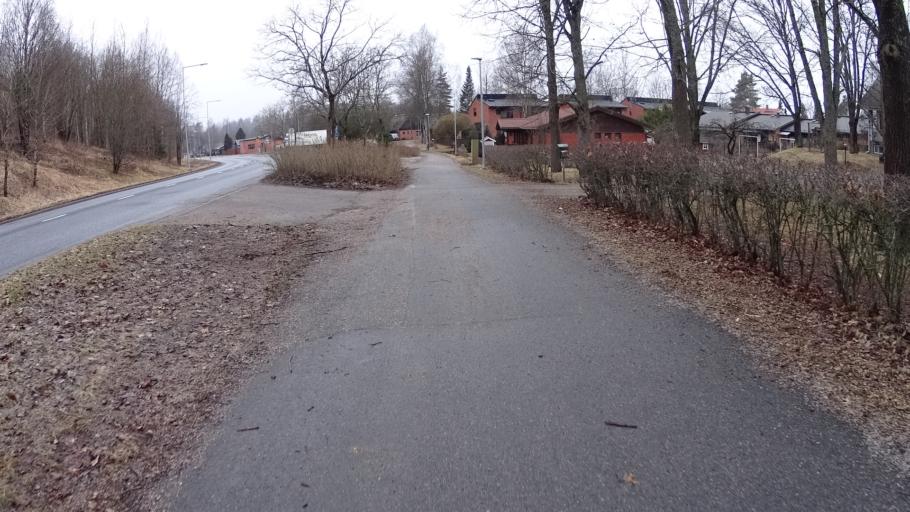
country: FI
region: Uusimaa
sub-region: Helsinki
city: Kilo
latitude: 60.2665
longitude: 24.8019
